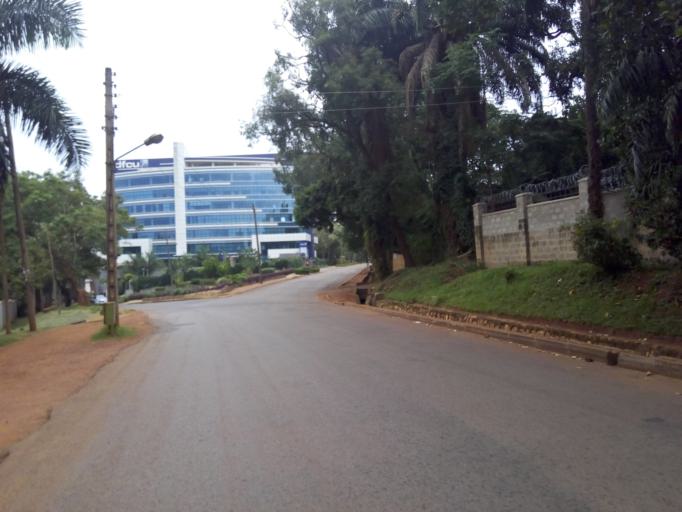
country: UG
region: Central Region
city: Kampala Central Division
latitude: 0.3274
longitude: 32.5817
